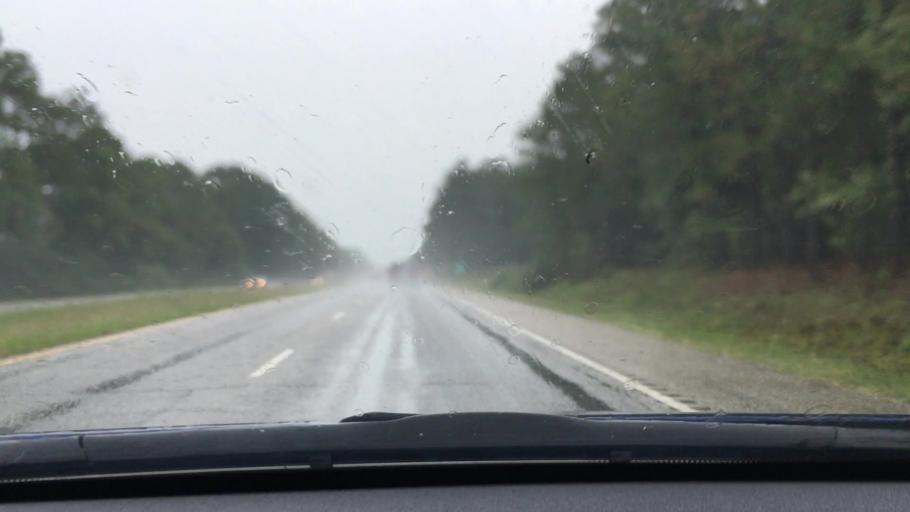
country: US
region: South Carolina
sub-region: Sumter County
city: Stateburg
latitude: 33.9457
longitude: -80.5310
